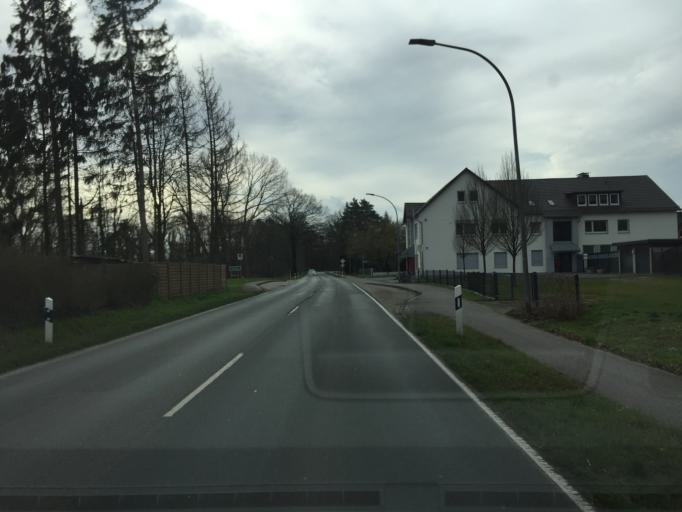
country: DE
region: North Rhine-Westphalia
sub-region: Regierungsbezirk Detmold
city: Lage
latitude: 51.9727
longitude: 8.8003
